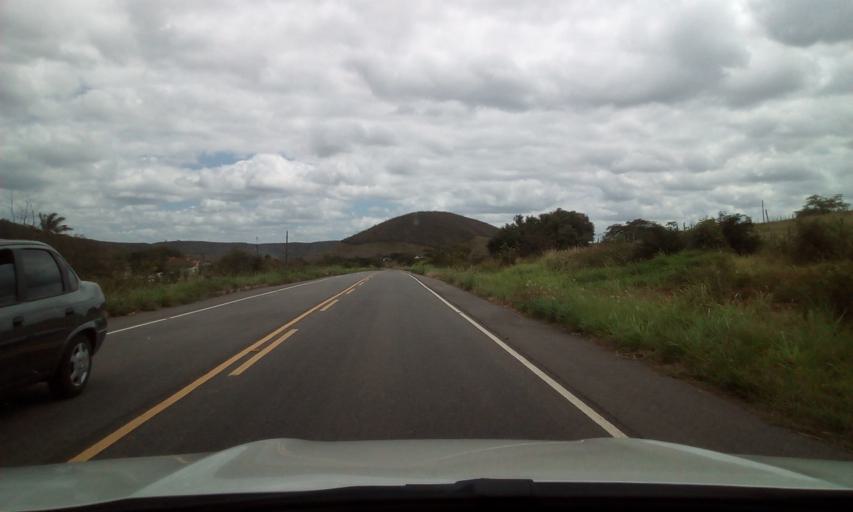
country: BR
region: Paraiba
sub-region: Serra Redonda
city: Alagoa Grande
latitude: -7.1240
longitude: -35.6146
